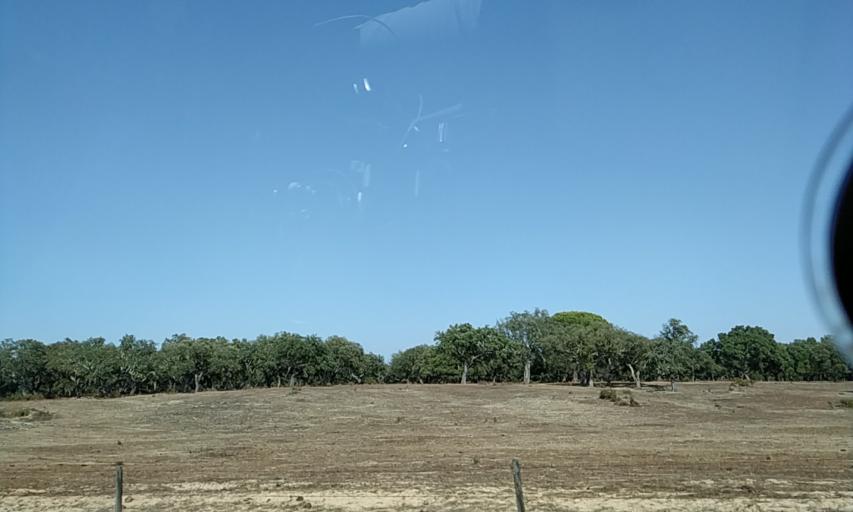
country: PT
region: Santarem
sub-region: Coruche
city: Coruche
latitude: 38.9161
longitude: -8.5249
